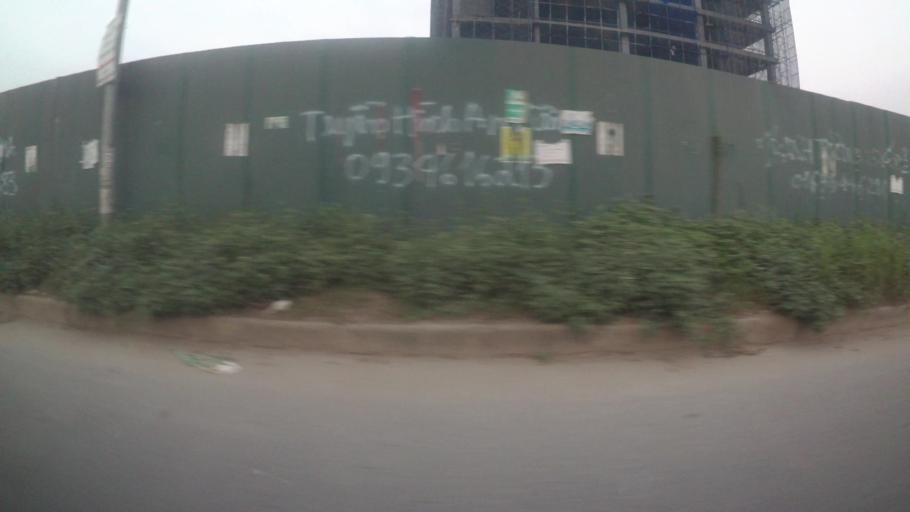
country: VN
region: Ha Noi
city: Tay Ho
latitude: 21.0645
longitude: 105.7900
